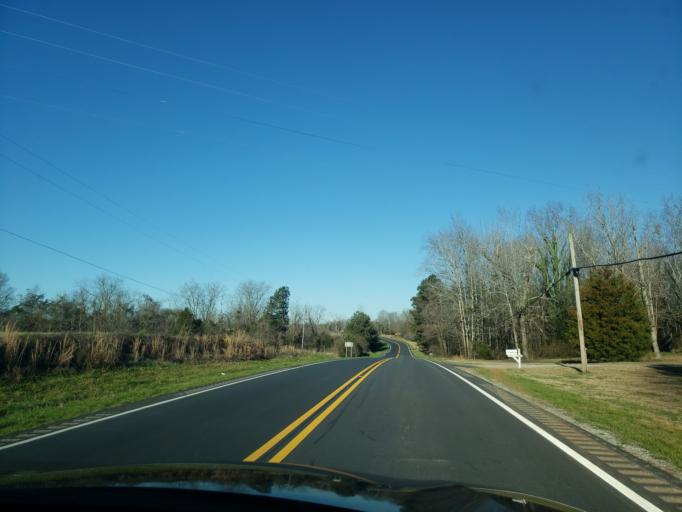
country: US
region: Alabama
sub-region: Macon County
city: Tuskegee
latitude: 32.5794
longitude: -85.7025
